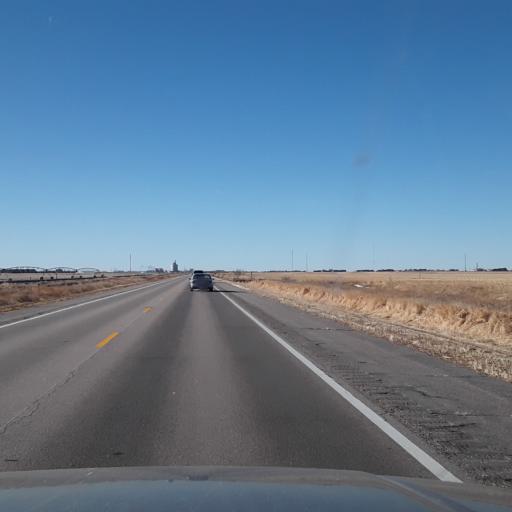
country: US
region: Nebraska
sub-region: Kearney County
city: Minden
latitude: 40.4910
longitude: -99.0348
